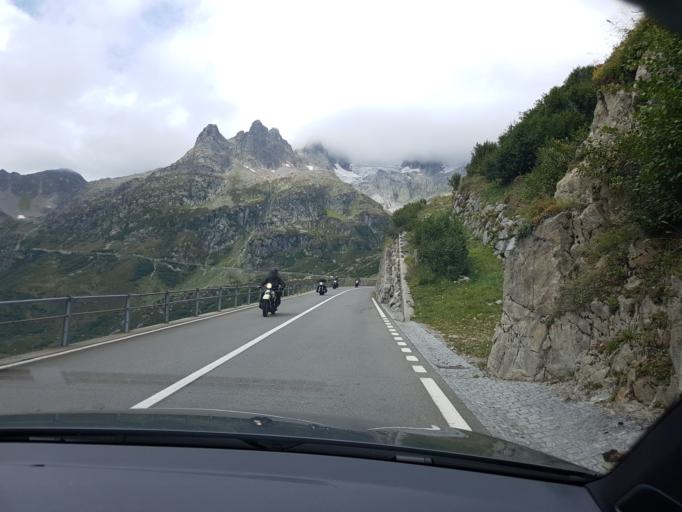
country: CH
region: Obwalden
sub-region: Obwalden
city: Engelberg
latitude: 46.7462
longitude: 8.4809
